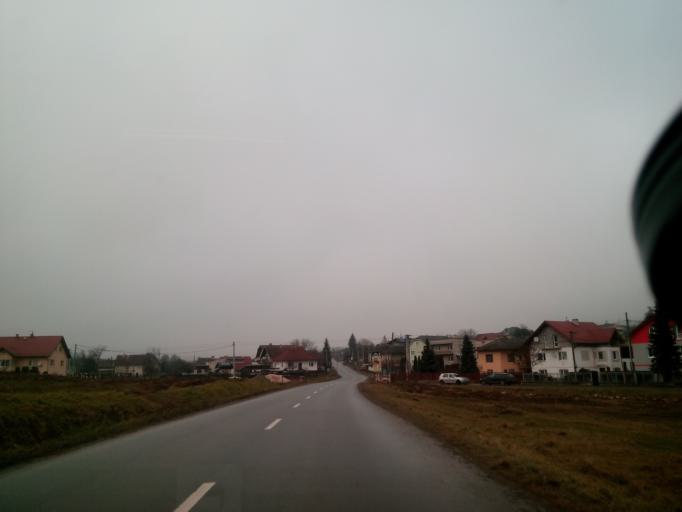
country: SK
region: Kosicky
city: Krompachy
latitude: 48.9646
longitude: 20.9556
